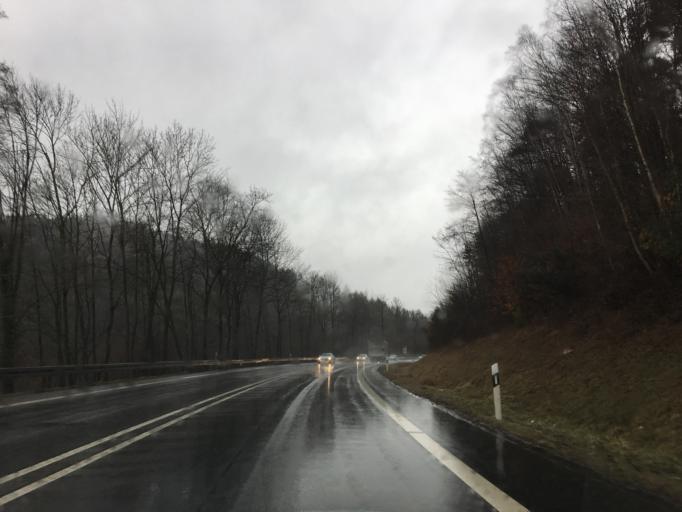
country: DE
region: Hesse
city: Michelstadt
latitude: 49.7006
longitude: 9.0000
